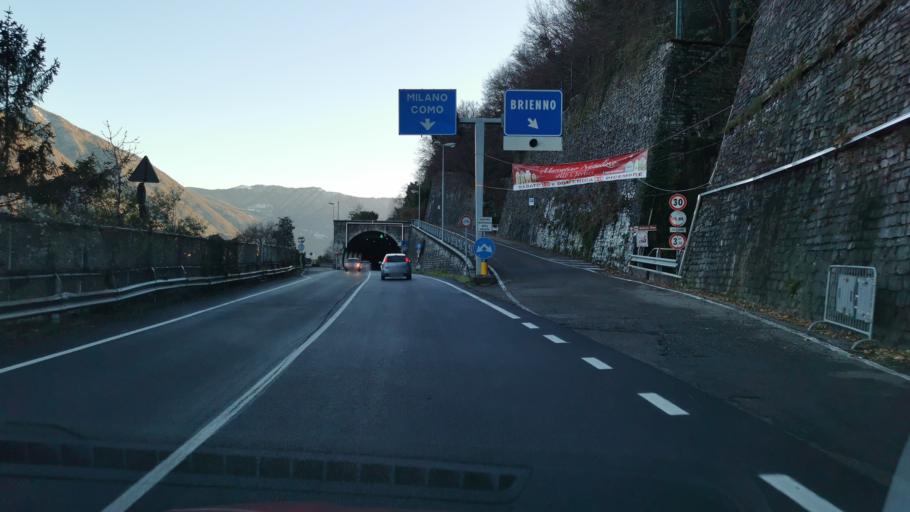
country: IT
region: Lombardy
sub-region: Provincia di Como
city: Brienno
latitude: 45.9202
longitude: 9.1314
